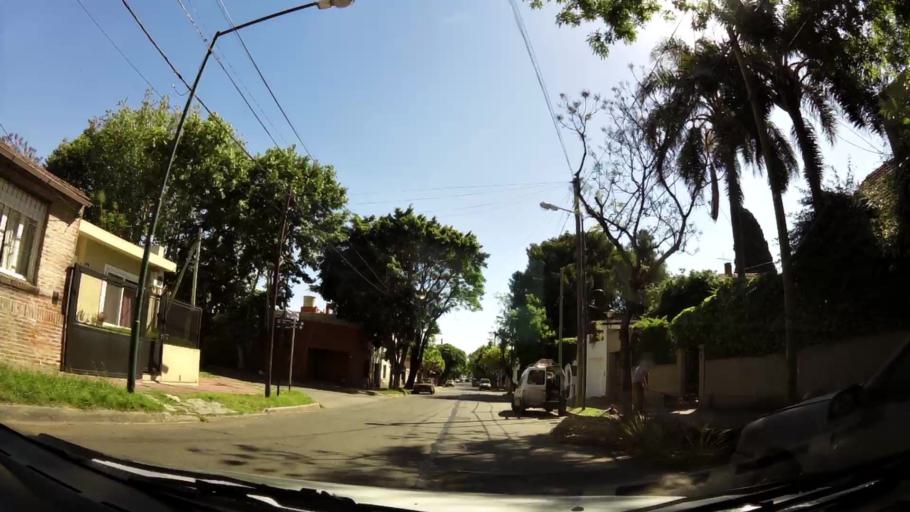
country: AR
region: Buenos Aires
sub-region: Partido de San Isidro
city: San Isidro
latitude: -34.4549
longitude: -58.5324
